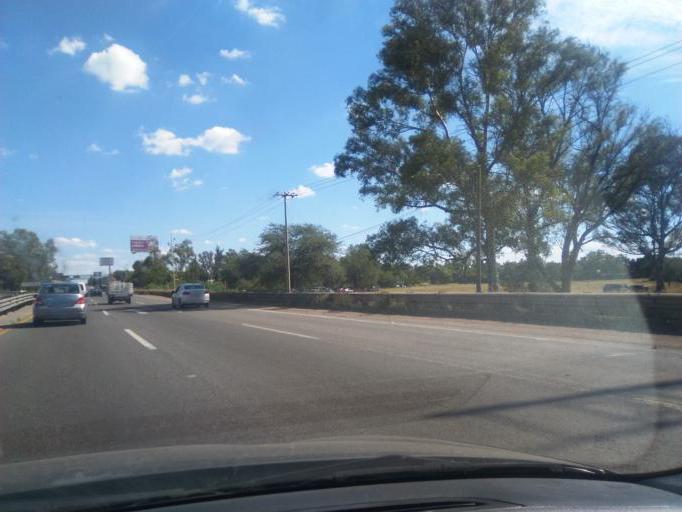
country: MX
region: Guanajuato
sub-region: Silao de la Victoria
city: El Refugio de los Sauces
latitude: 21.0274
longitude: -101.5427
